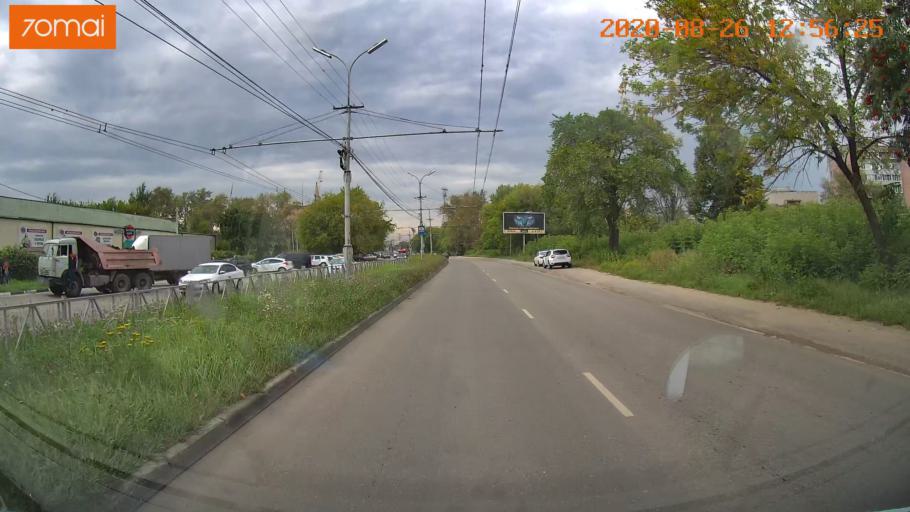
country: RU
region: Rjazan
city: Ryazan'
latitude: 54.6134
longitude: 39.7504
